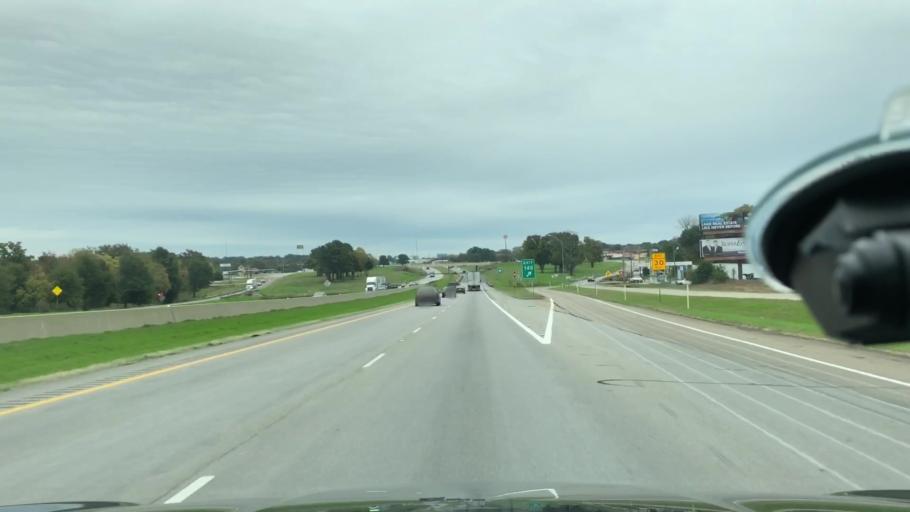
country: US
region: Texas
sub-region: Franklin County
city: Mount Vernon
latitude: 33.1623
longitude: -95.2417
